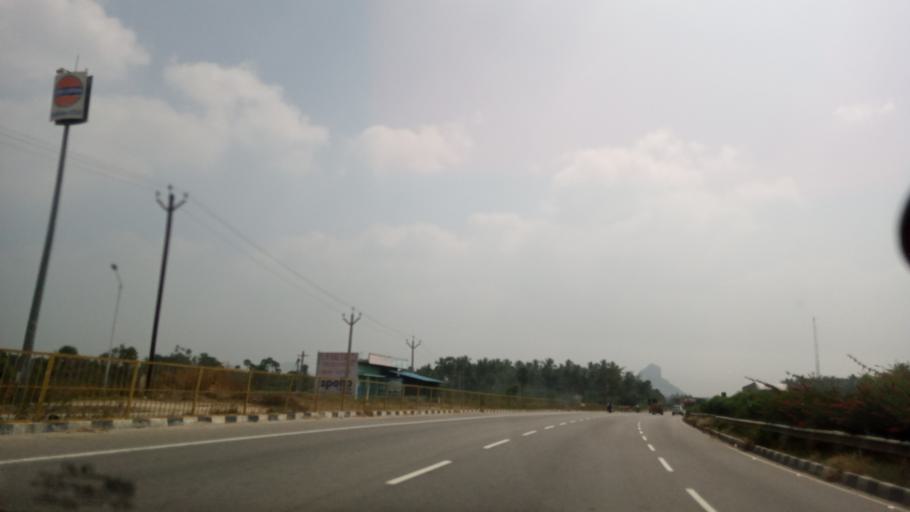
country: IN
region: Tamil Nadu
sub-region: Krishnagiri
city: Krishnagiri
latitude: 12.5705
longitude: 78.1735
